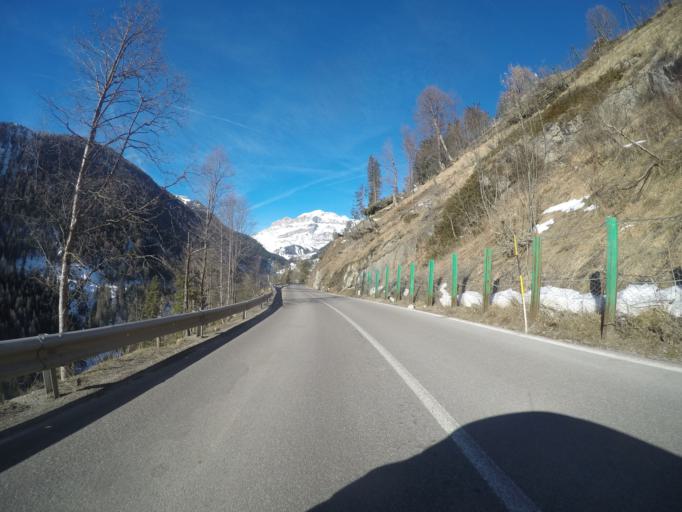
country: IT
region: Veneto
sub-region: Provincia di Belluno
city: Livinallongo del Col di Lana
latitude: 46.4951
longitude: 11.9271
